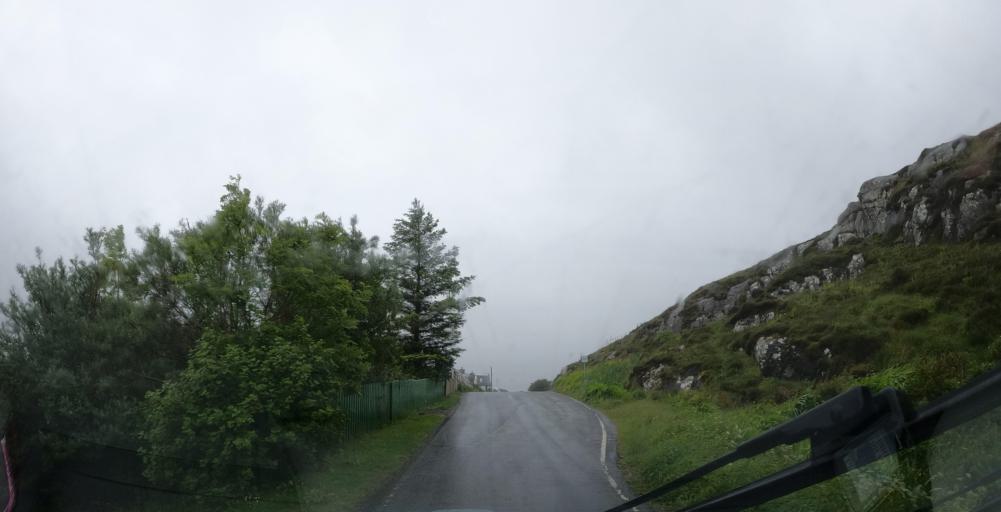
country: GB
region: Scotland
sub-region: Eilean Siar
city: Barra
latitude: 57.0110
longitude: -7.4319
